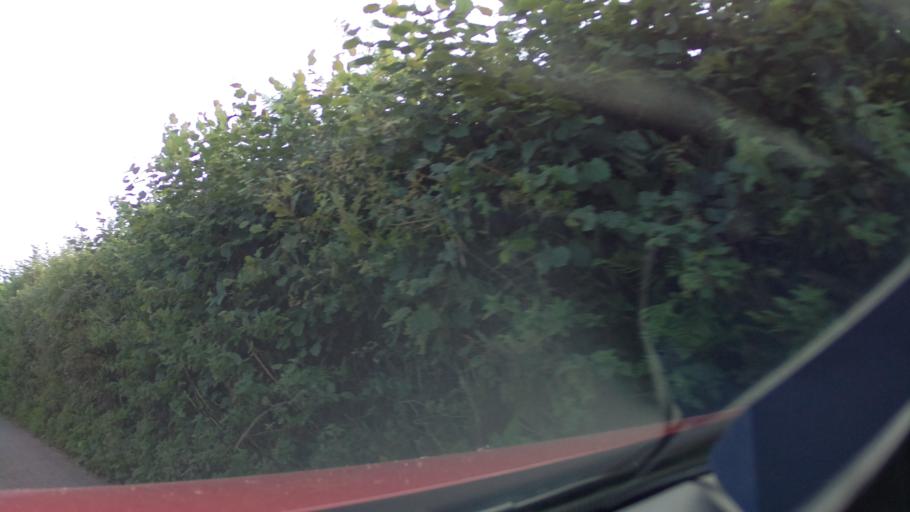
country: GB
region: England
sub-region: Devon
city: Totnes
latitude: 50.4246
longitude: -3.7299
